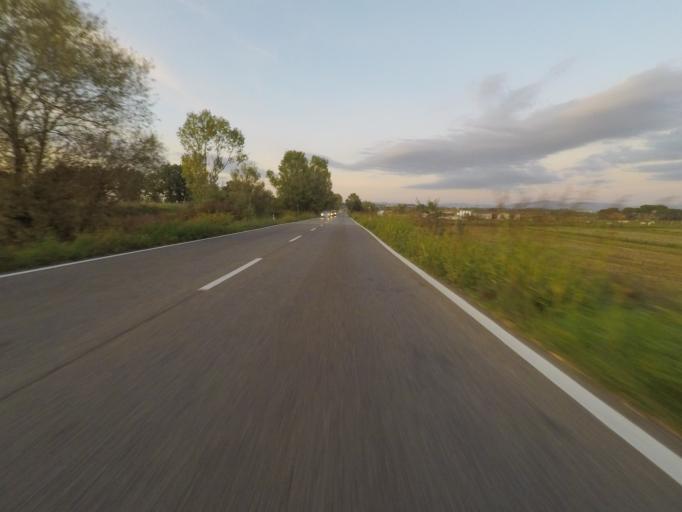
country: IT
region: Tuscany
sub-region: Provincia di Siena
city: Sinalunga
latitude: 43.1919
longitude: 11.7588
